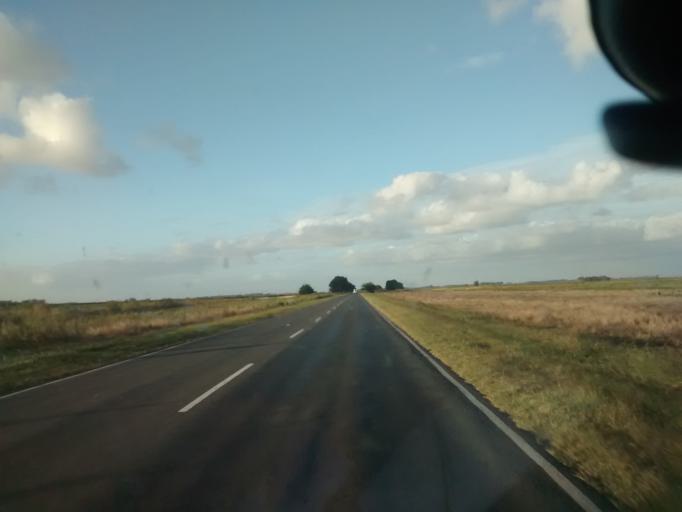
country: AR
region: Buenos Aires
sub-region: Partido de General Belgrano
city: General Belgrano
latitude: -35.8394
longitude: -58.5898
